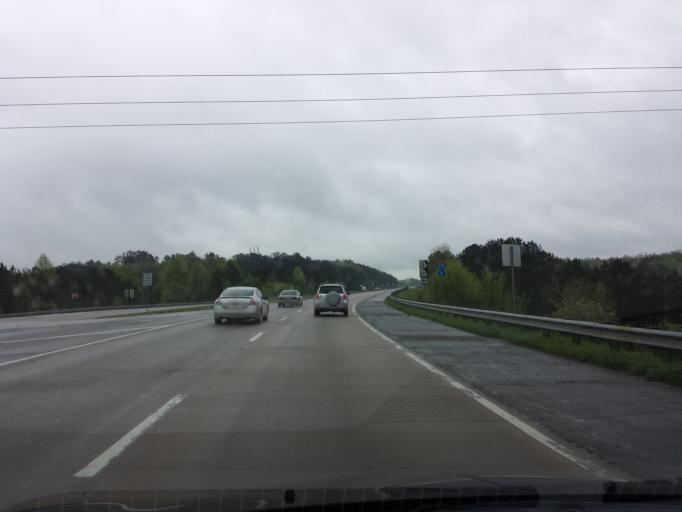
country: US
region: Georgia
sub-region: Pickens County
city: Nelson
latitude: 34.3817
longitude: -84.3941
